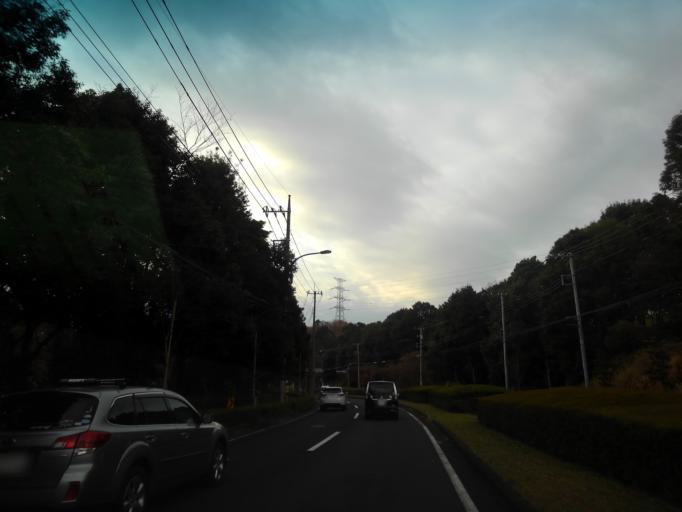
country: JP
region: Tokyo
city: Hino
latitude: 35.6189
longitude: 139.4427
